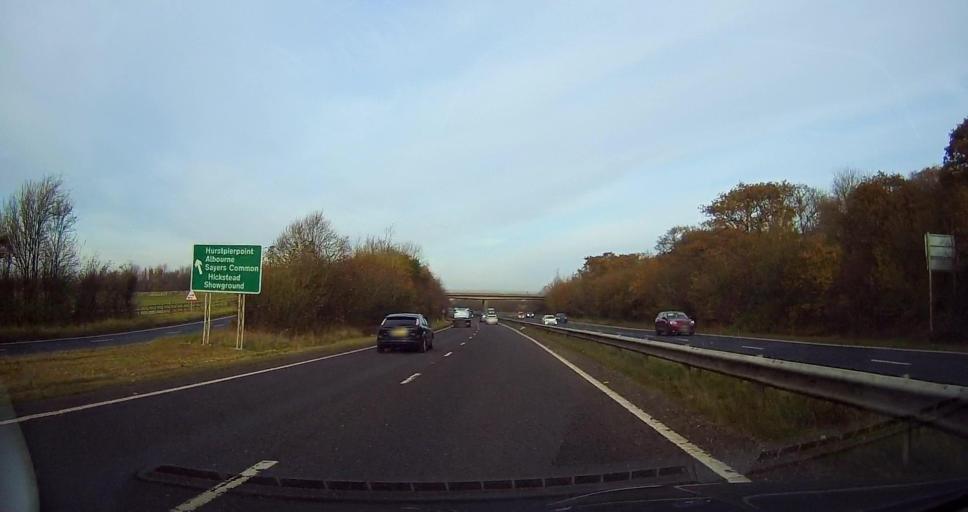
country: GB
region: England
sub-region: West Sussex
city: Hurstpierpoint
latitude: 50.9189
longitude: -0.1923
